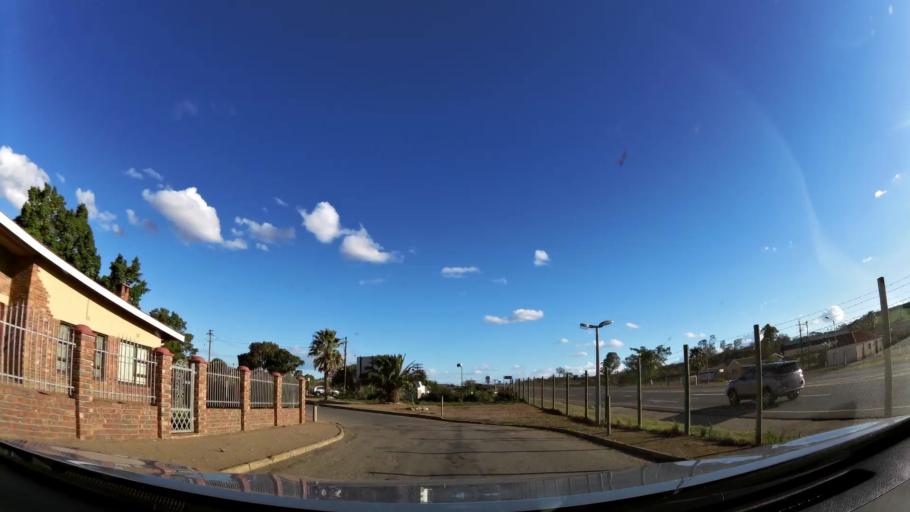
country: ZA
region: Western Cape
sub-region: Eden District Municipality
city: Riversdale
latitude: -34.1001
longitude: 20.9616
